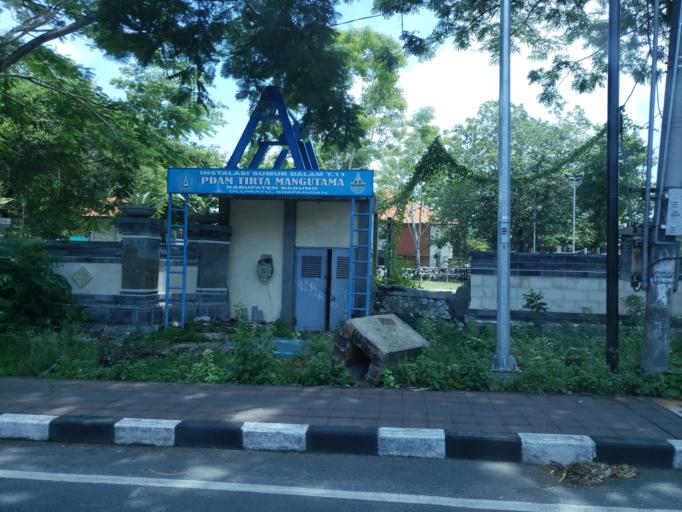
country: ID
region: Bali
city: Jimbaran
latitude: -8.8001
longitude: 115.1606
